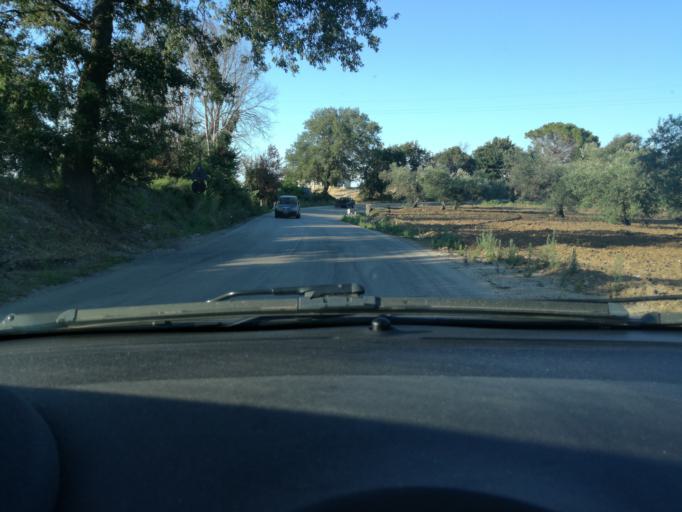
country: IT
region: Molise
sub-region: Provincia di Campobasso
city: Guglionesi
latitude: 41.9255
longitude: 14.9215
